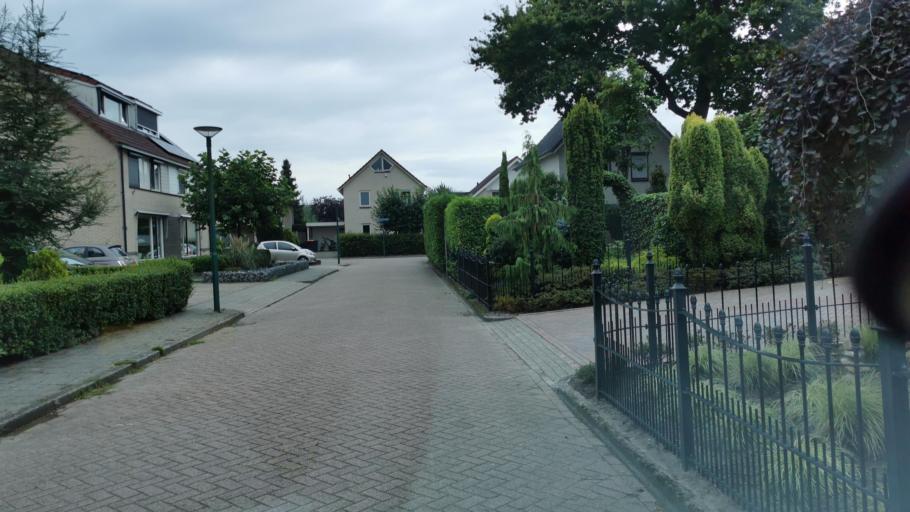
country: NL
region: Overijssel
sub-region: Gemeente Losser
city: Losser
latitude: 52.2196
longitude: 6.9590
